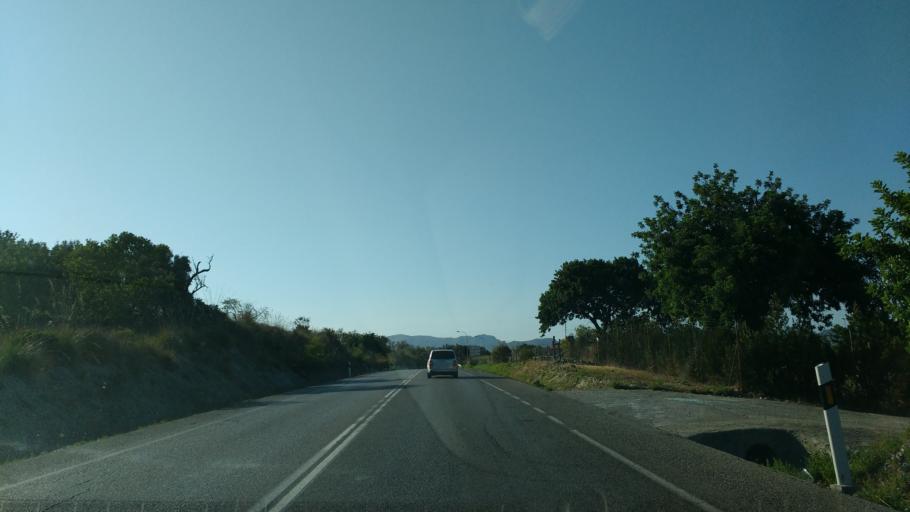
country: ES
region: Balearic Islands
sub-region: Illes Balears
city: Alcudia
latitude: 39.8395
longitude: 3.0997
